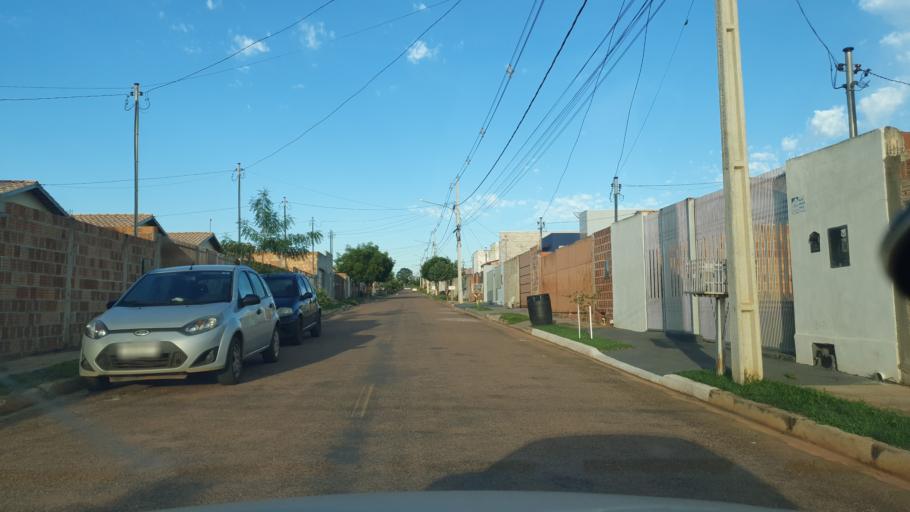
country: BR
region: Mato Grosso
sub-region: Pontes E Lacerda
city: Pontes e Lacerda
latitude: -15.2278
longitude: -59.3109
